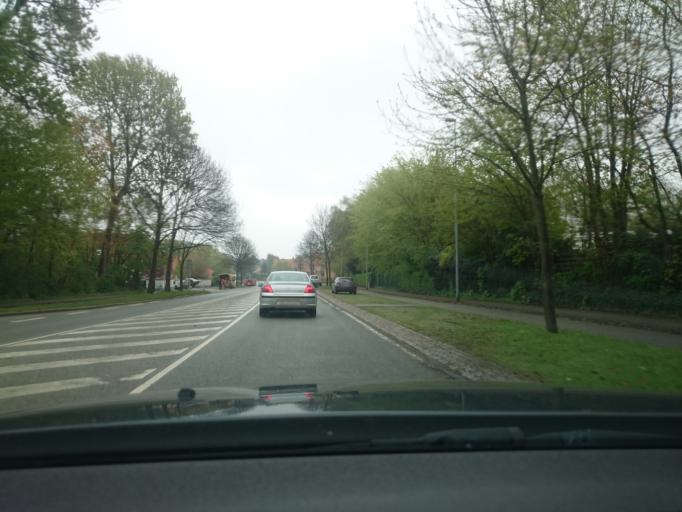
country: DK
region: Capital Region
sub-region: Gladsaxe Municipality
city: Buddinge
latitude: 55.7653
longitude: 12.4517
